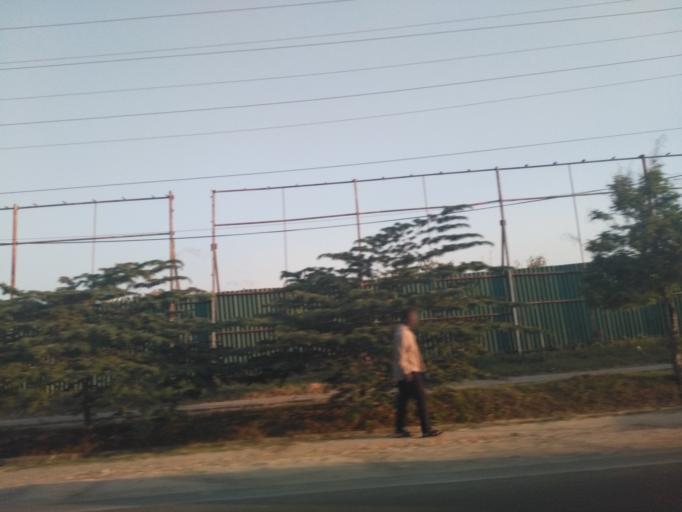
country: TZ
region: Dar es Salaam
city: Dar es Salaam
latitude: -6.8588
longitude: 39.2158
